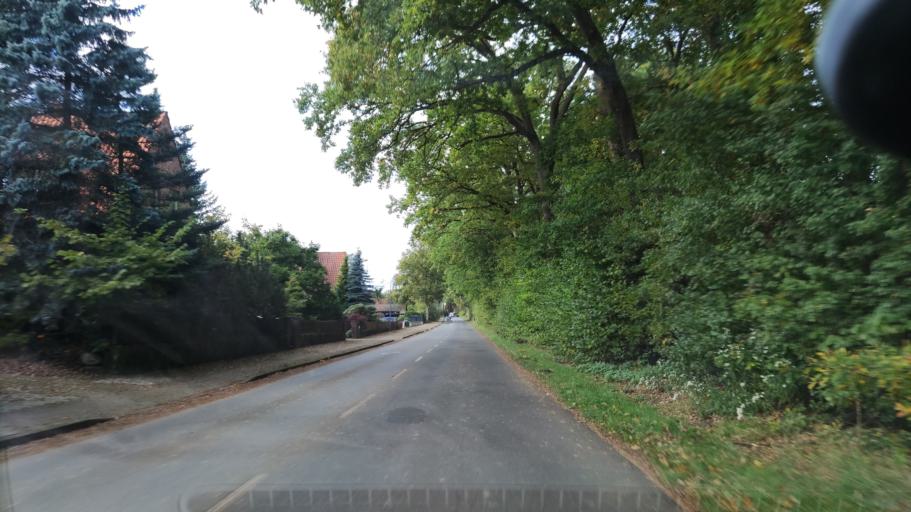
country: DE
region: Lower Saxony
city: Jelmstorf
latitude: 53.1036
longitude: 10.5478
